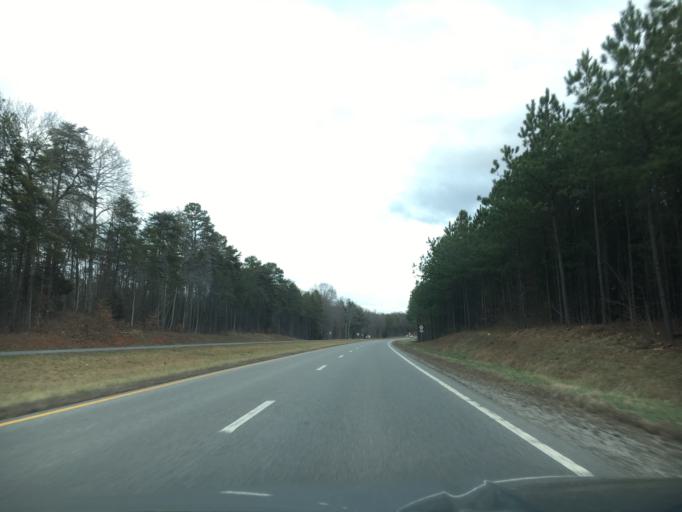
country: US
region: Virginia
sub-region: Prince Edward County
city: Hampden Sydney
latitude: 37.0853
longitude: -78.4108
